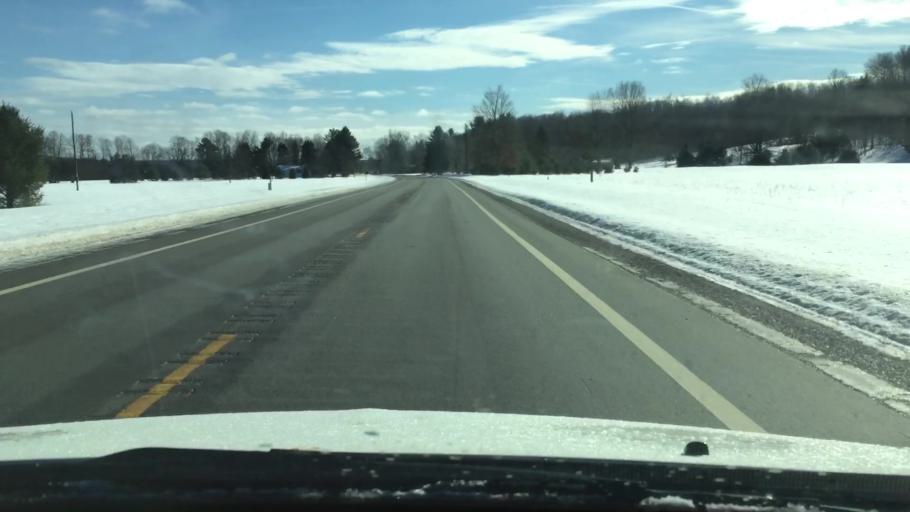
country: US
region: Michigan
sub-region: Charlevoix County
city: East Jordan
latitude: 45.0699
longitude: -85.0851
